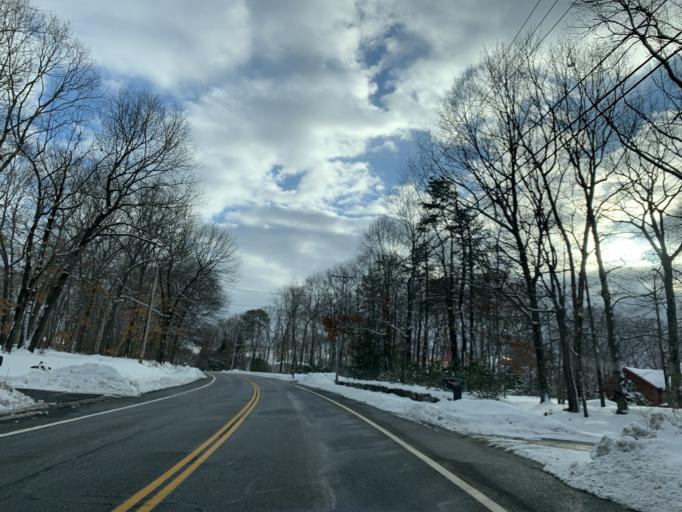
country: US
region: Rhode Island
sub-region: Providence County
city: Cumberland Hill
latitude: 42.0008
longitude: -71.4562
